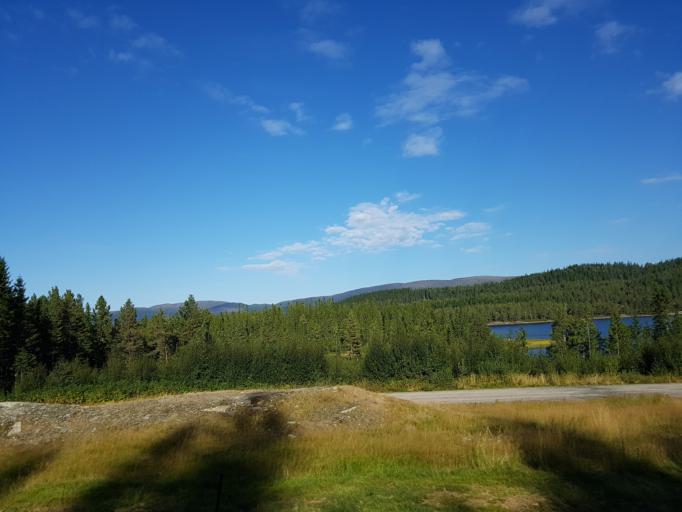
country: NO
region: Sor-Trondelag
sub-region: Trondheim
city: Trondheim
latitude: 63.6282
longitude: 10.2518
